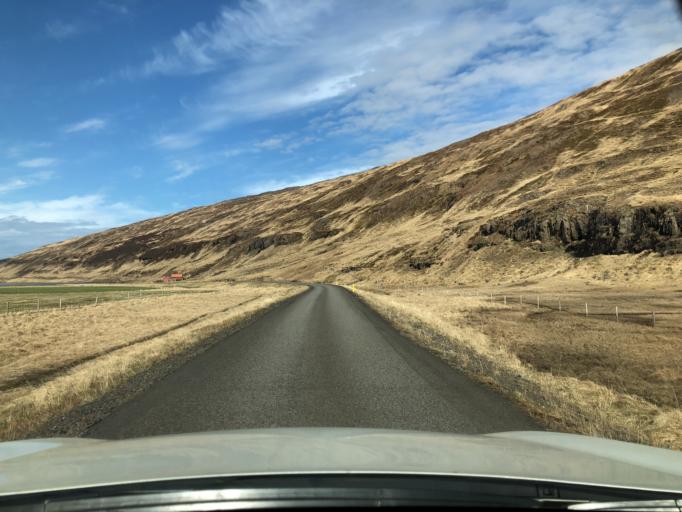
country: IS
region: West
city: Borgarnes
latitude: 65.0581
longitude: -21.5673
